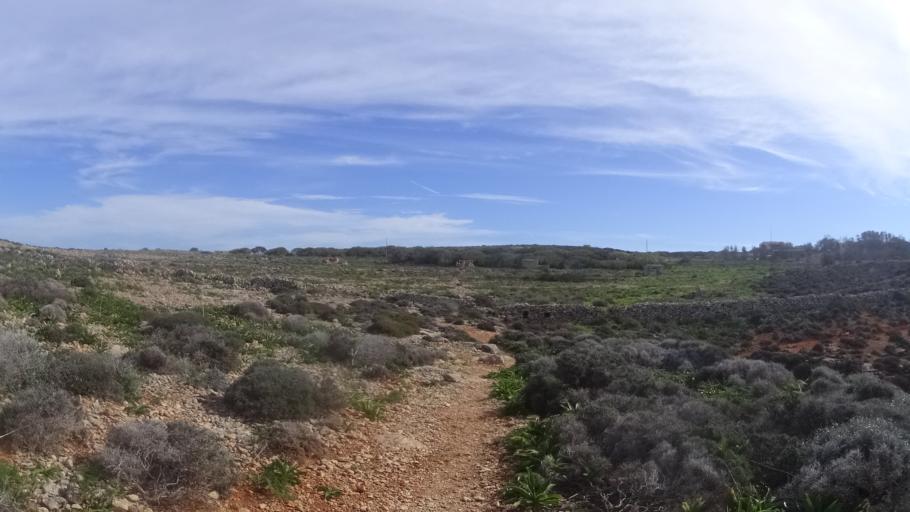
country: MT
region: Il-Qala
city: Qala
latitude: 36.0101
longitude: 14.3299
